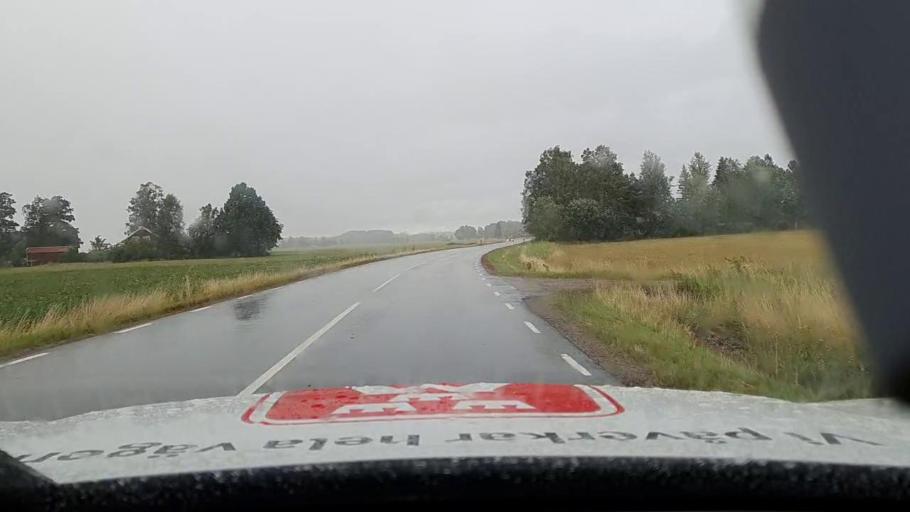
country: SE
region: Vaestra Goetaland
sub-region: Toreboda Kommun
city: Toereboda
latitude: 58.6619
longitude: 14.1275
